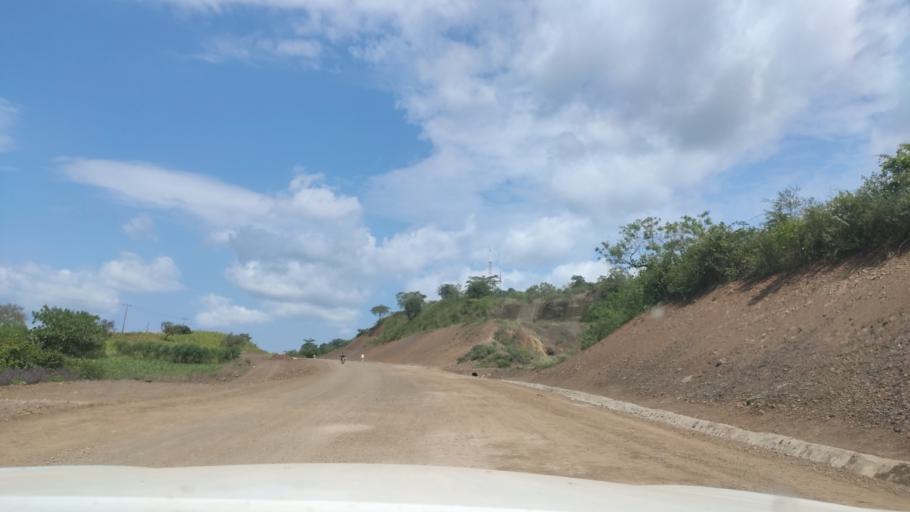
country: ET
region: Southern Nations, Nationalities, and People's Region
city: Felege Neway
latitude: 6.3910
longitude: 37.0675
